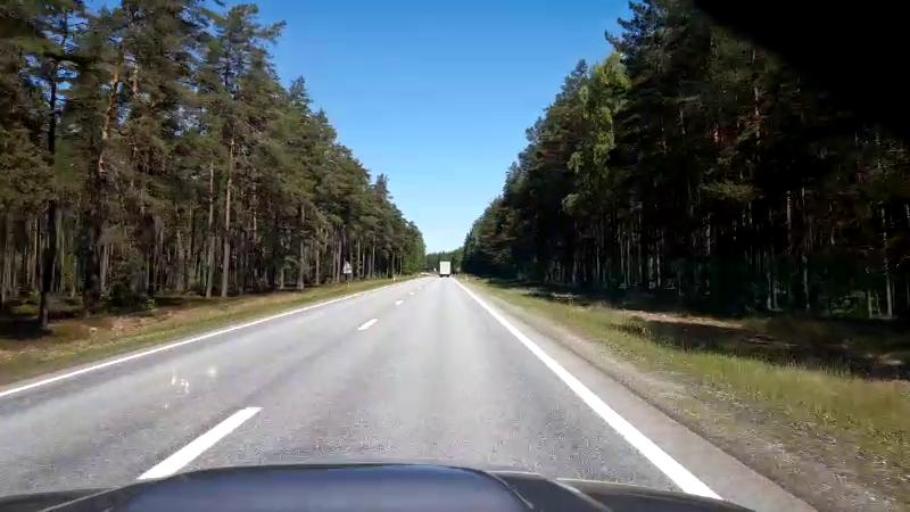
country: LV
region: Salacgrivas
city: Salacgriva
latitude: 57.5669
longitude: 24.4344
